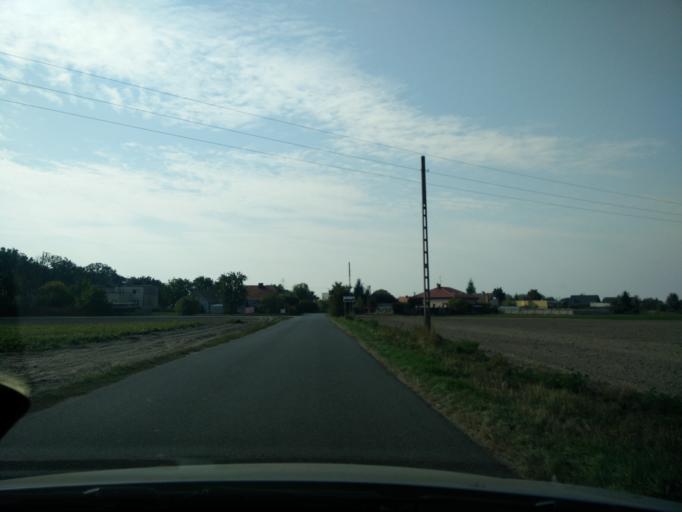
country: PL
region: Greater Poland Voivodeship
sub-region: Powiat sredzki
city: Dominowo
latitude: 52.3048
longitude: 17.2904
